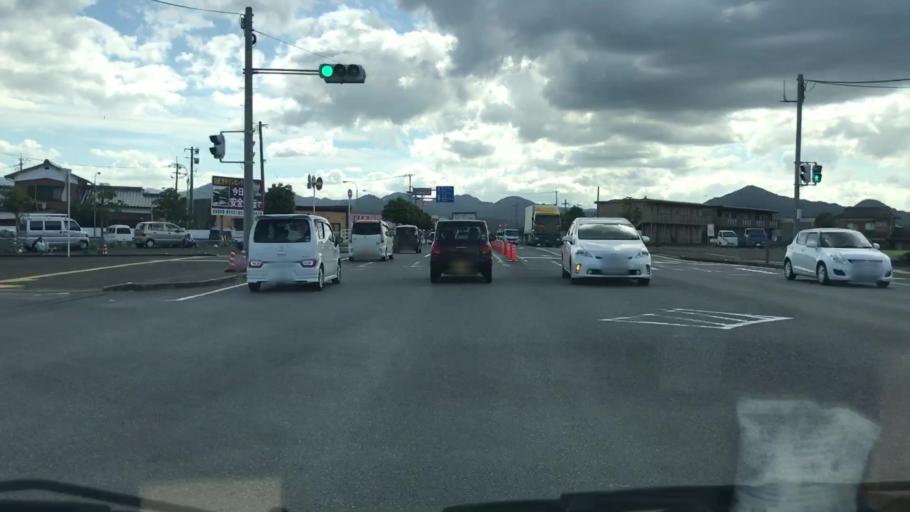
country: JP
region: Saga Prefecture
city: Kashima
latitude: 33.1273
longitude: 130.1033
